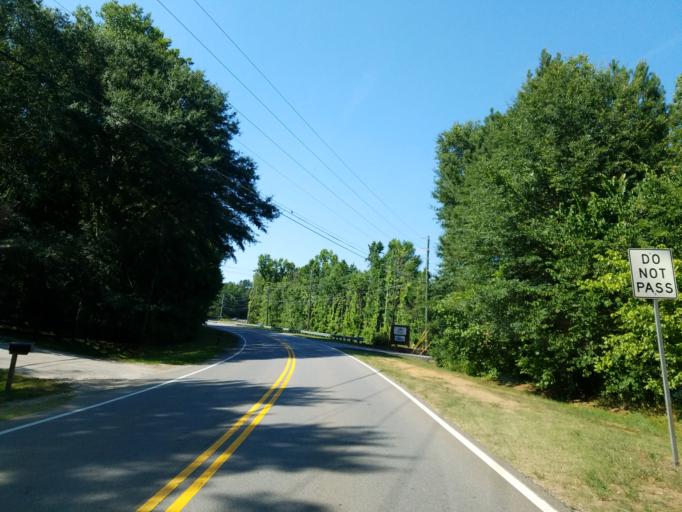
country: US
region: Georgia
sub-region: Fulton County
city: Milton
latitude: 34.1280
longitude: -84.3436
